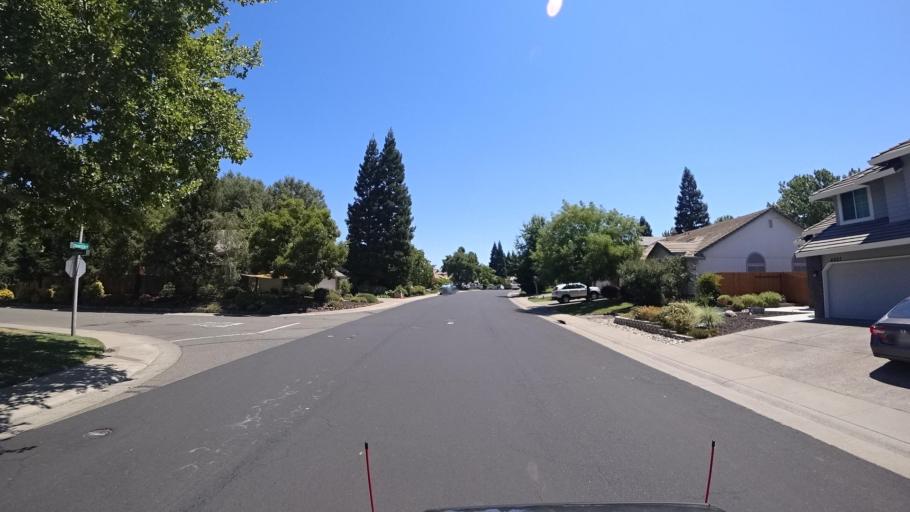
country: US
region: California
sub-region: Placer County
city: Rocklin
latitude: 38.8261
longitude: -121.2526
